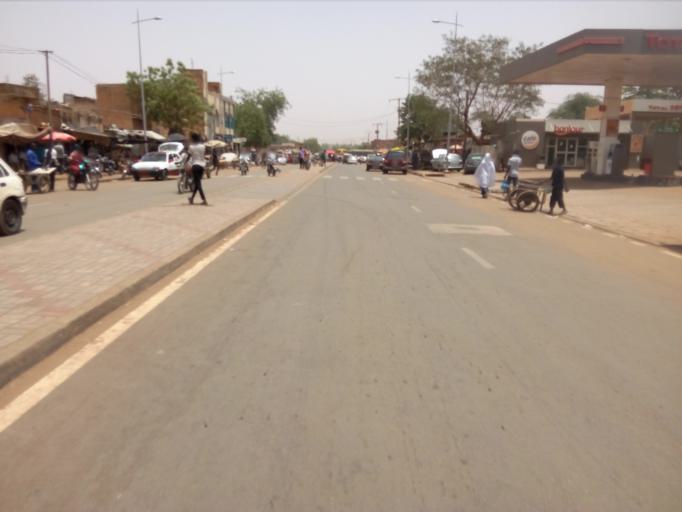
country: NE
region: Niamey
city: Niamey
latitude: 13.5235
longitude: 2.1201
